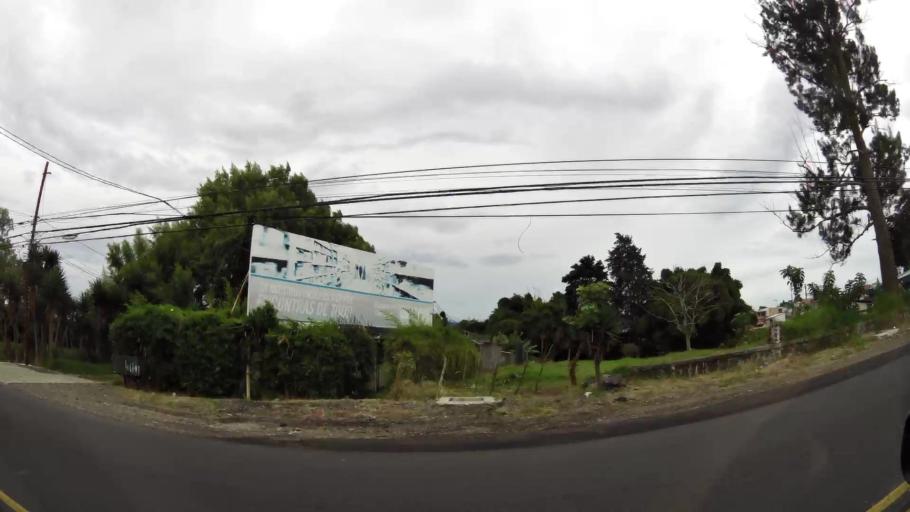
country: CR
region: San Jose
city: Ipis
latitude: 9.9685
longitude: -84.0202
